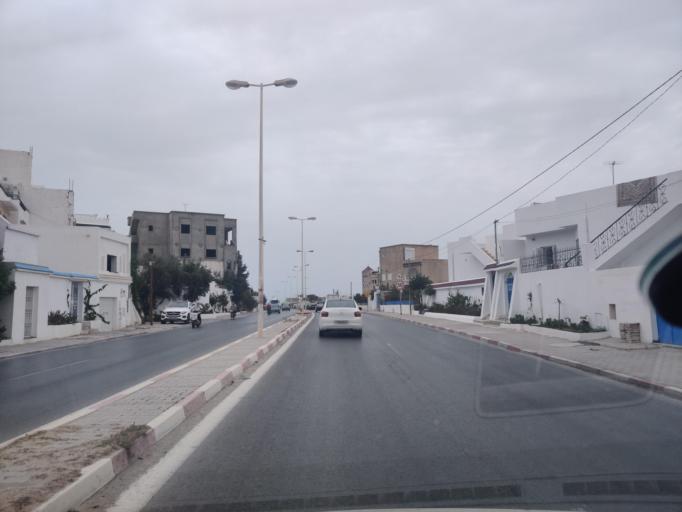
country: TN
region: Nabul
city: Al Hammamat
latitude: 36.4085
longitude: 10.6289
